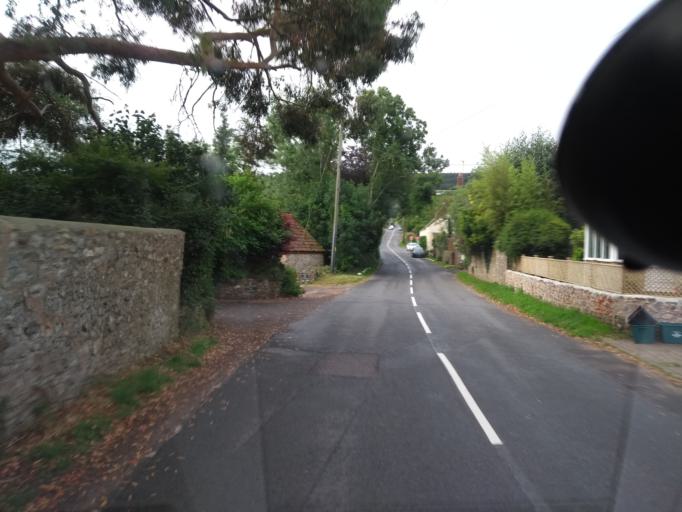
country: GB
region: England
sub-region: Somerset
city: Taunton
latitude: 50.9594
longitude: -3.1243
